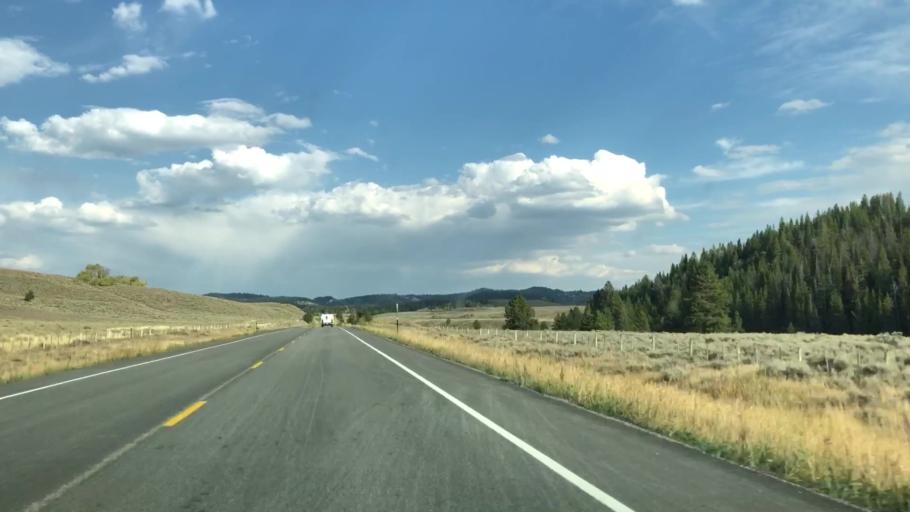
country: US
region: Wyoming
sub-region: Sublette County
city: Pinedale
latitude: 43.1513
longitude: -110.2788
